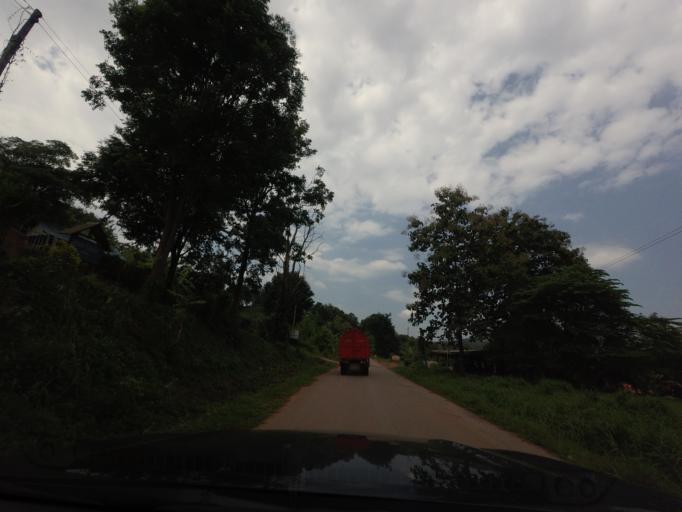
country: TH
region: Uttaradit
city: Fak Tha
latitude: 17.8052
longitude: 100.9332
